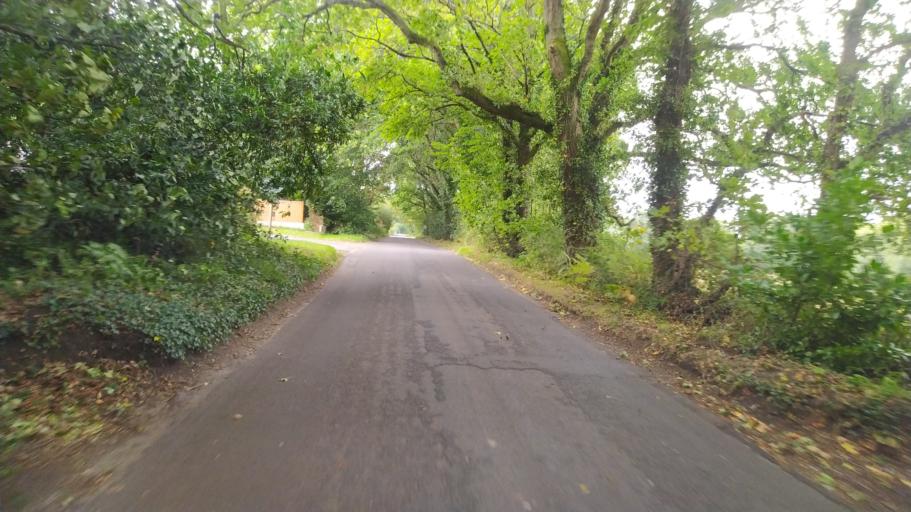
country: GB
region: England
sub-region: Dorset
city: Broadstone
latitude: 50.7644
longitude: -2.0299
